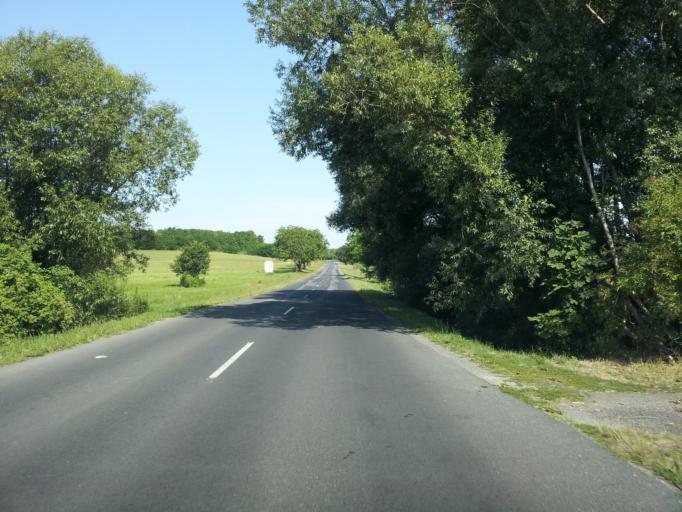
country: HU
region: Zala
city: Cserszegtomaj
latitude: 46.8331
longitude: 17.1921
